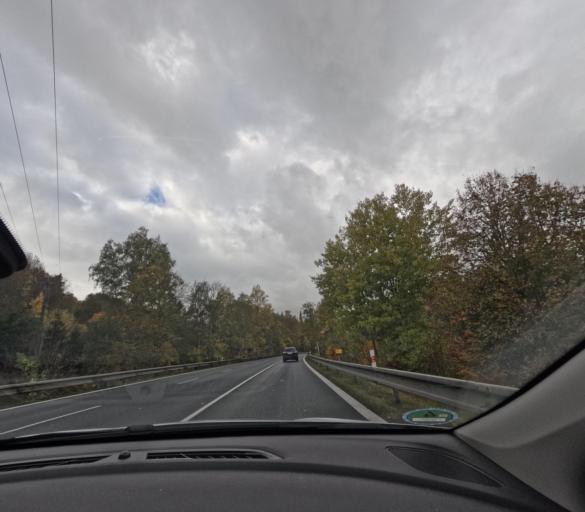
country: CZ
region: Karlovarsky
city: Dalovice
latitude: 50.2335
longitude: 12.9077
